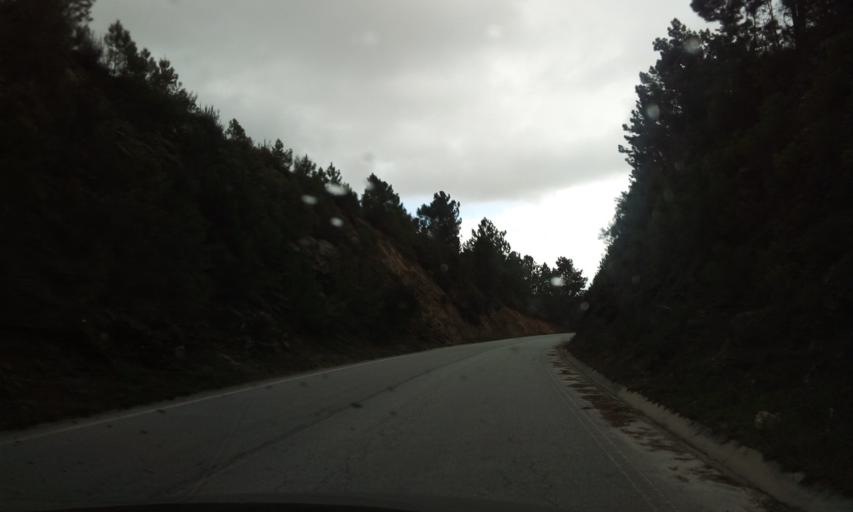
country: PT
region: Guarda
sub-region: Fornos de Algodres
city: Fornos de Algodres
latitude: 40.6300
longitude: -7.6076
